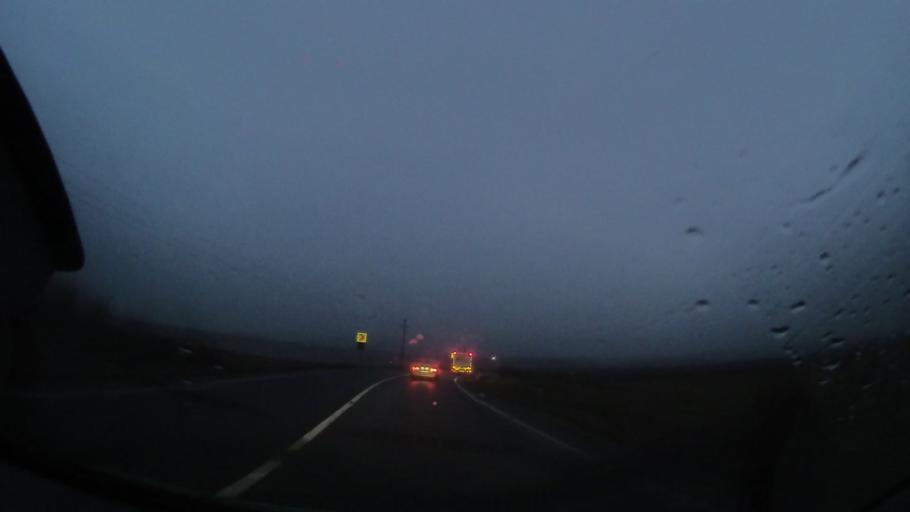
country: RO
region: Harghita
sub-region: Comuna Ditrau
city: Ditrau
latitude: 46.8223
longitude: 25.4922
